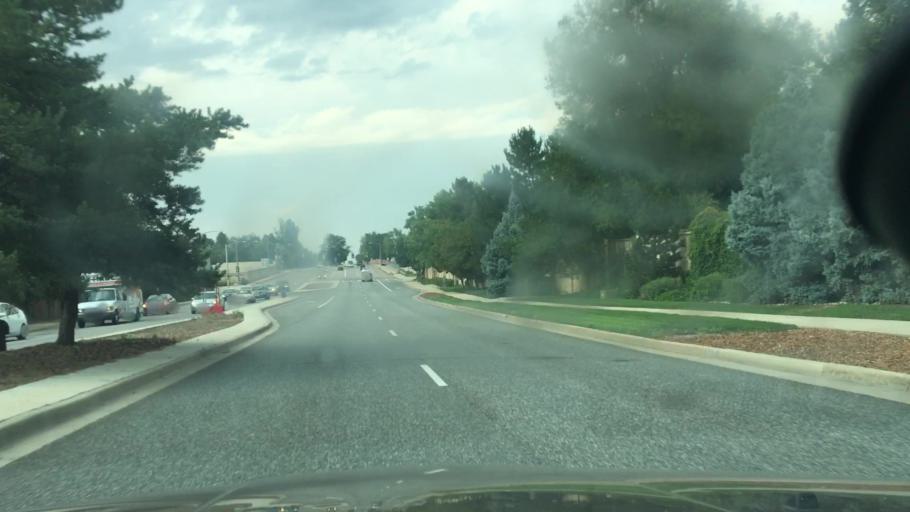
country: US
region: Colorado
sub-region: Arapahoe County
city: Castlewood
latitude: 39.6372
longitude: -104.8851
